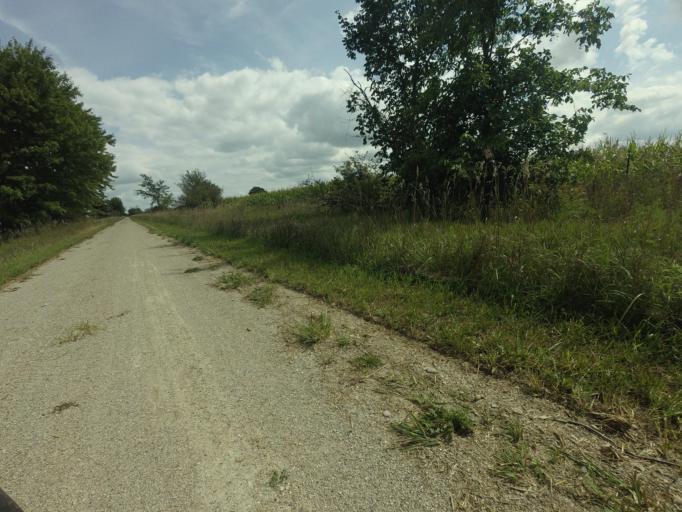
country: CA
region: Ontario
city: North Perth
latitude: 43.5708
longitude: -80.8829
